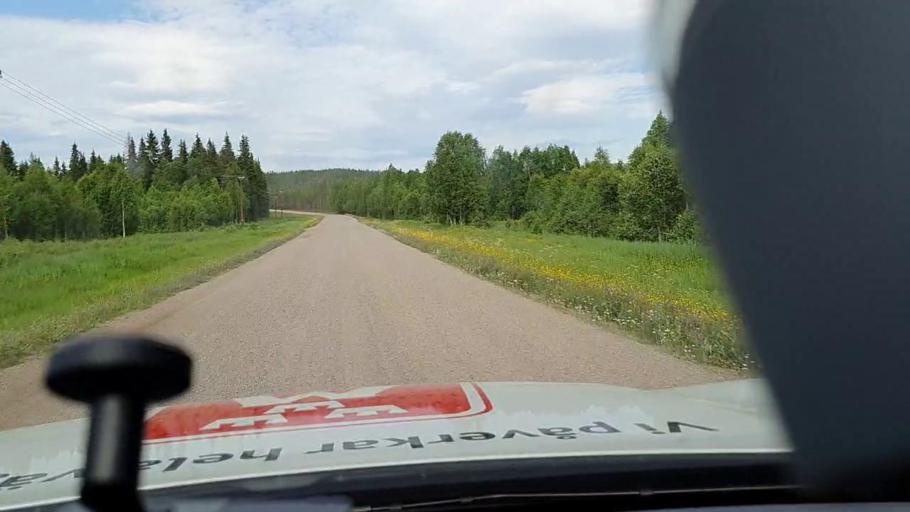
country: SE
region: Norrbotten
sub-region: Alvsbyns Kommun
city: AElvsbyn
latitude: 66.1199
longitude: 20.9849
